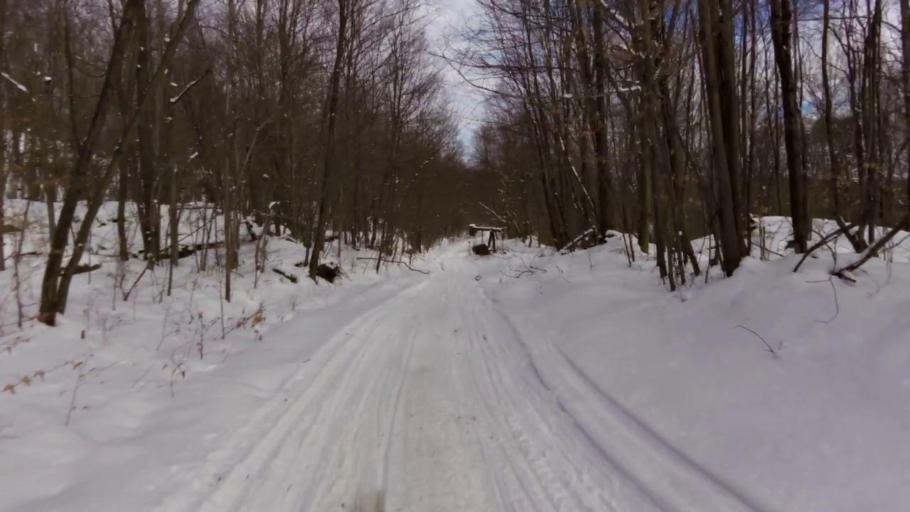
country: US
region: Pennsylvania
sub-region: McKean County
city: Foster Brook
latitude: 42.0151
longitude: -78.5557
